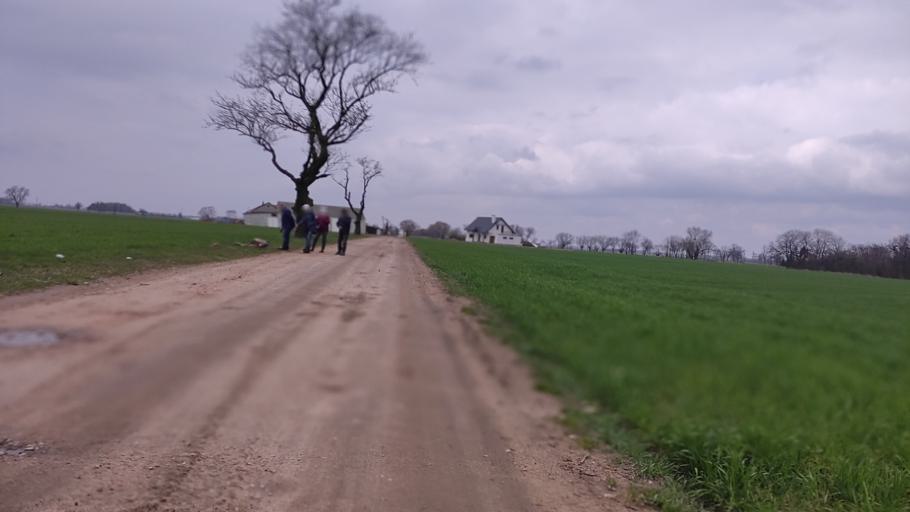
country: PL
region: Greater Poland Voivodeship
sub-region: Powiat poznanski
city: Swarzedz
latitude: 52.4050
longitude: 17.1416
